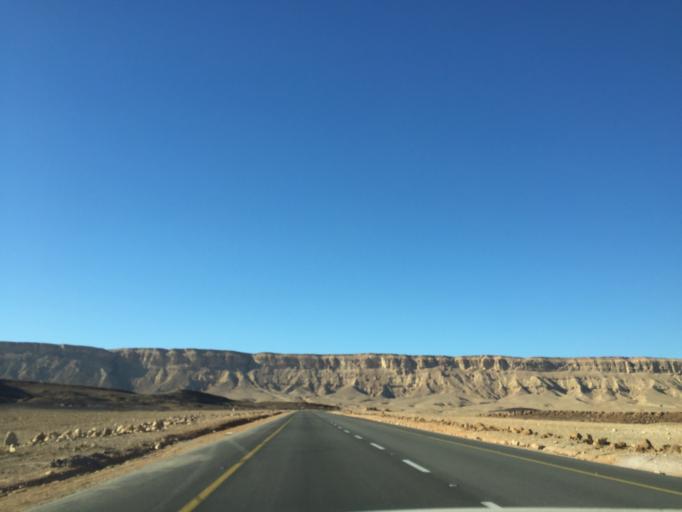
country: IL
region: Southern District
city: Mitzpe Ramon
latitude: 30.6184
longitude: 34.8464
